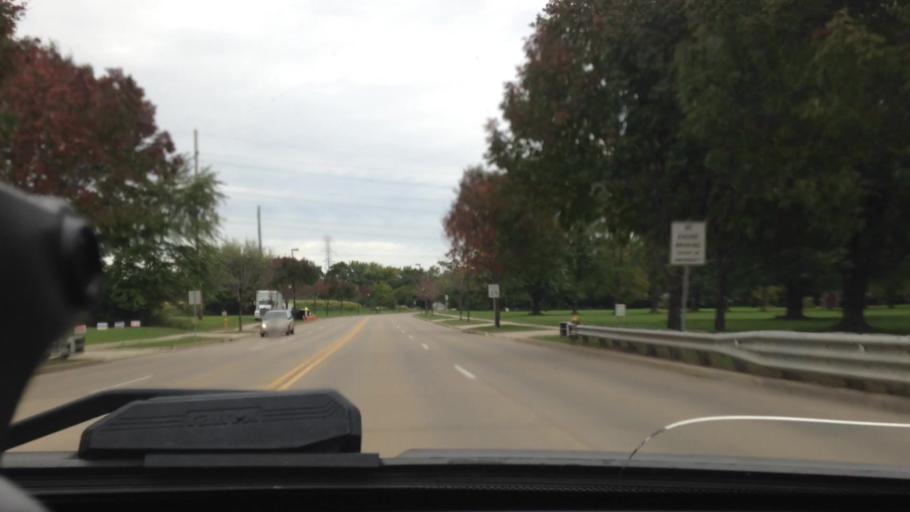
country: US
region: Wisconsin
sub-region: Fond du Lac County
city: North Fond du Lac
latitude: 43.7965
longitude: -88.4770
